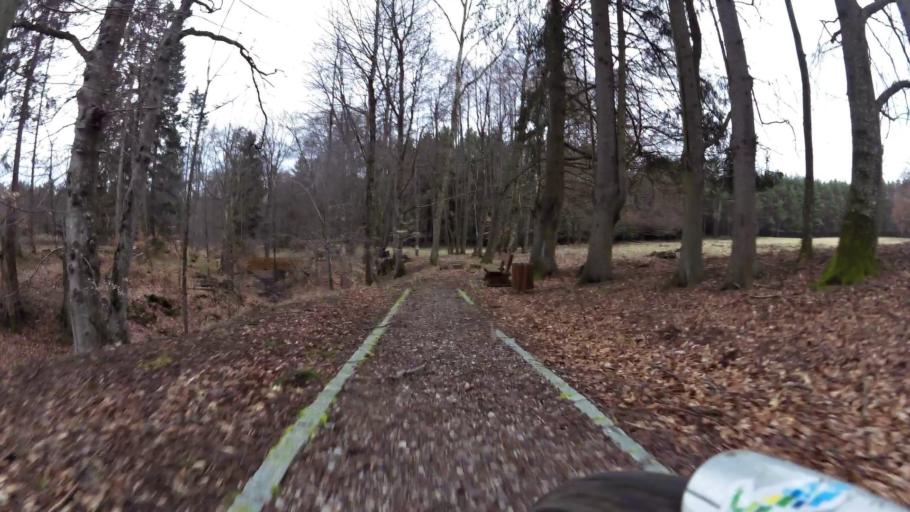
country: PL
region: Pomeranian Voivodeship
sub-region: Powiat bytowski
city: Trzebielino
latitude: 54.1410
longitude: 17.1479
